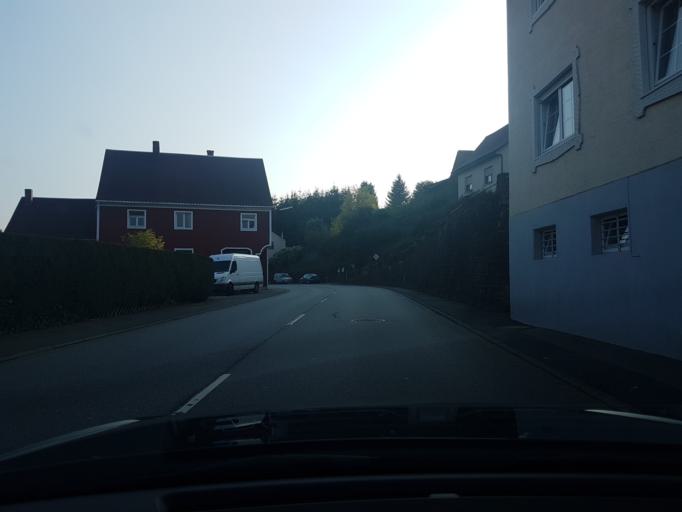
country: DE
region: Hesse
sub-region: Regierungsbezirk Darmstadt
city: Beerfelden
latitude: 49.5899
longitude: 8.9875
